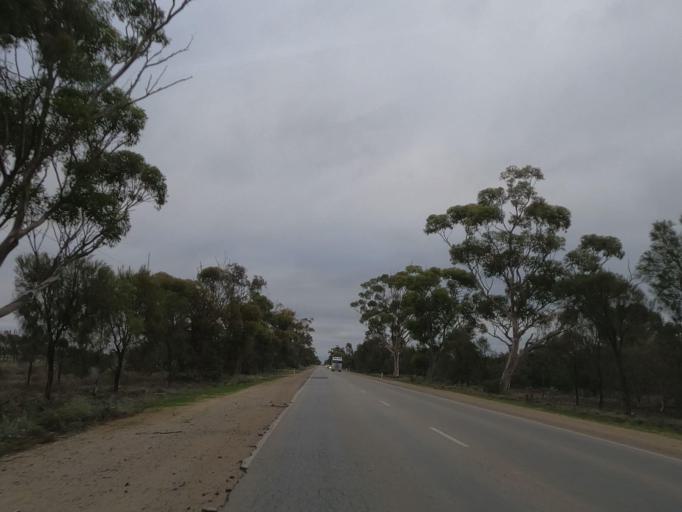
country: AU
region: Victoria
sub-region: Swan Hill
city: Swan Hill
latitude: -35.4107
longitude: 143.5853
